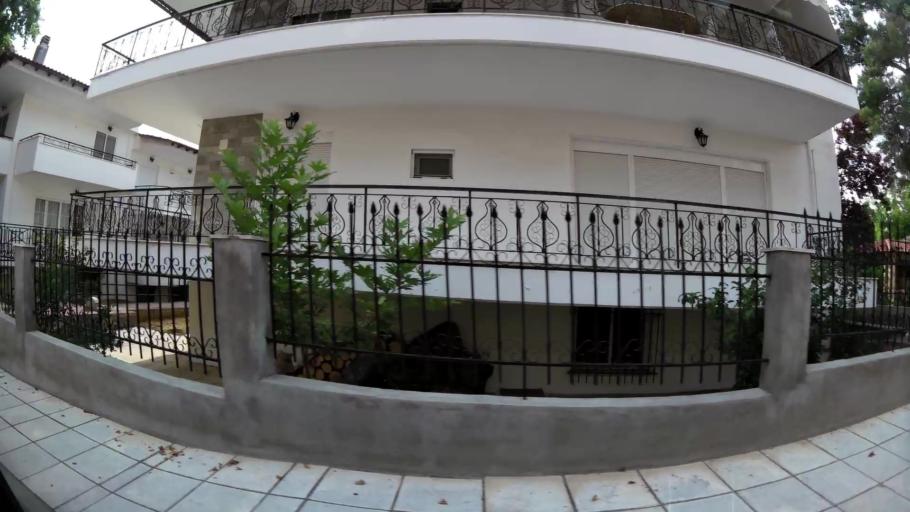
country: GR
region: Central Macedonia
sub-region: Nomos Thessalonikis
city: Oraiokastro
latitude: 40.7271
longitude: 22.9135
